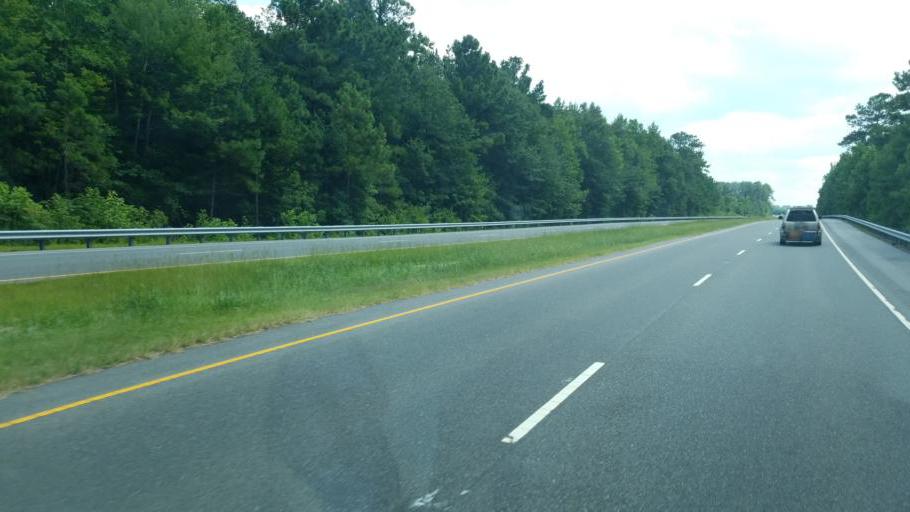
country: US
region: North Carolina
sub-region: Currituck County
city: Moyock
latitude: 36.6300
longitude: -76.2154
